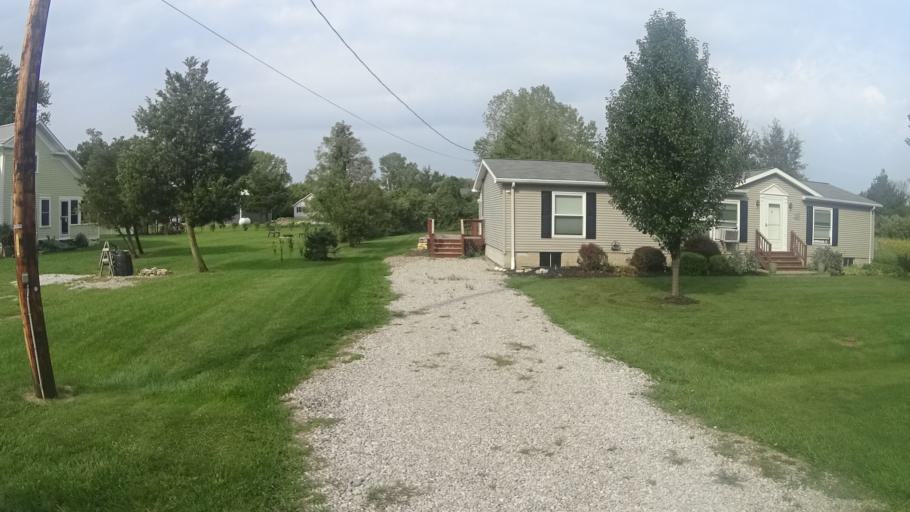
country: US
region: Ohio
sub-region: Erie County
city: Sandusky
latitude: 41.5907
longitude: -82.6884
